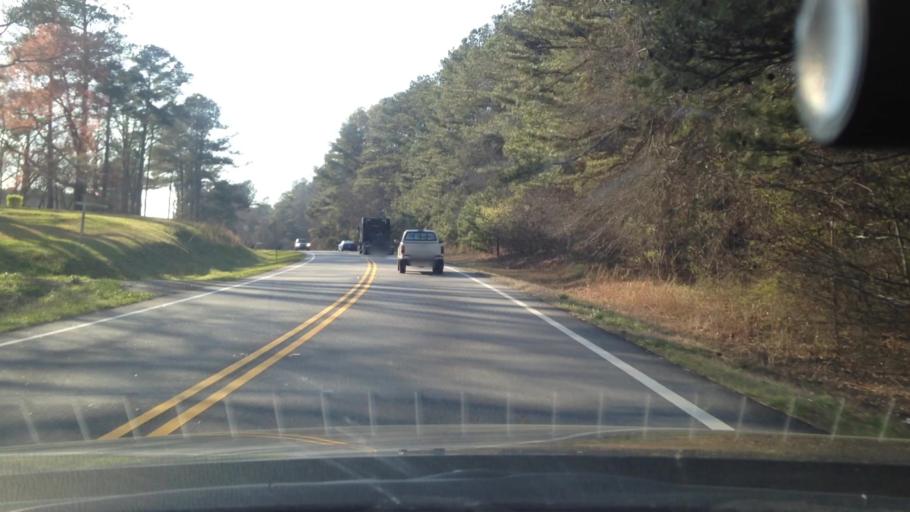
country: US
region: Georgia
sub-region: Fayette County
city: Peachtree City
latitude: 33.3391
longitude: -84.6533
